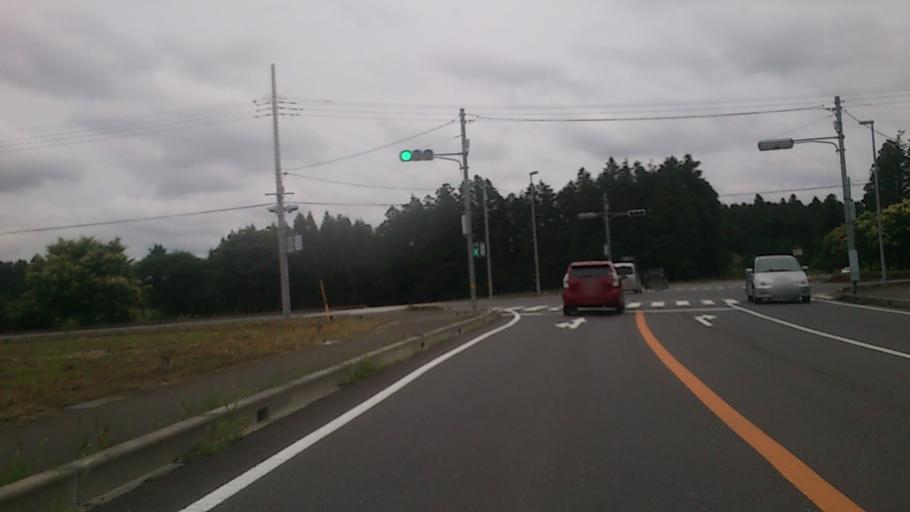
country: JP
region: Ibaraki
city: Ishioka
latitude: 36.2345
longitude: 140.3232
